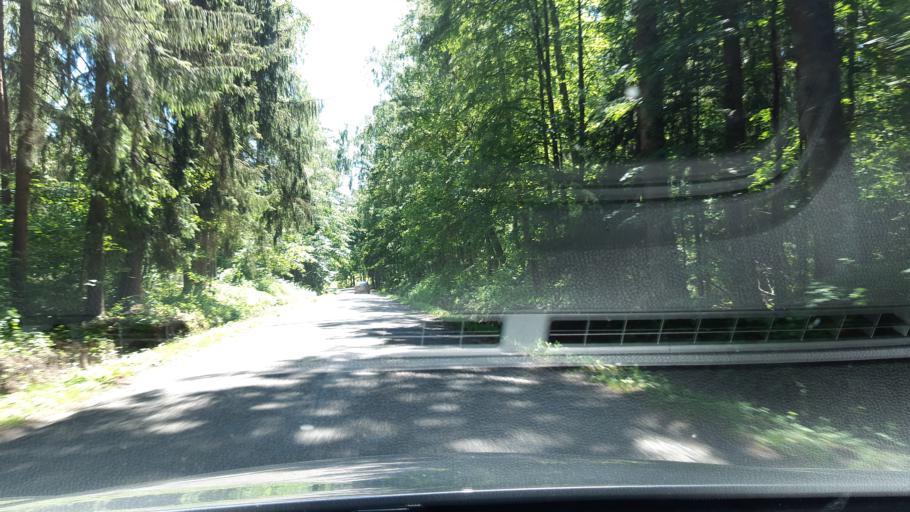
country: PL
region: Warmian-Masurian Voivodeship
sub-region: Powiat gizycki
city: Gizycko
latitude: 53.9503
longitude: 21.7408
